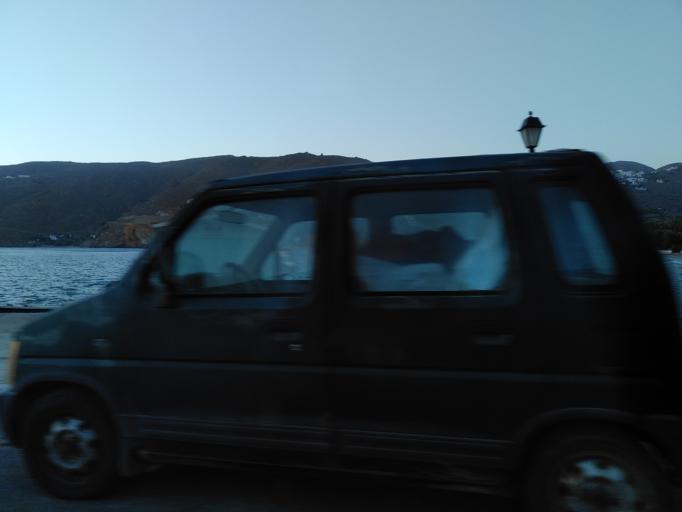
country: GR
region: South Aegean
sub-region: Nomos Kykladon
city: Amorgos
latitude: 36.9016
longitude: 25.9772
